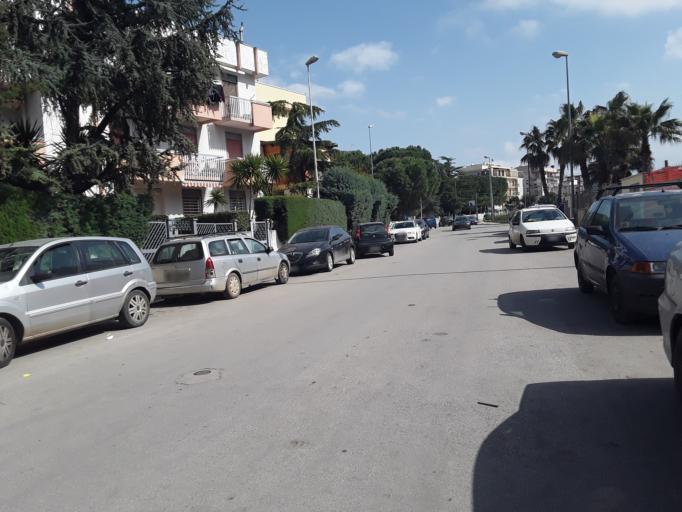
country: IT
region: Apulia
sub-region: Provincia di Bari
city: Ruvo di Puglia
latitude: 41.1233
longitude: 16.4803
